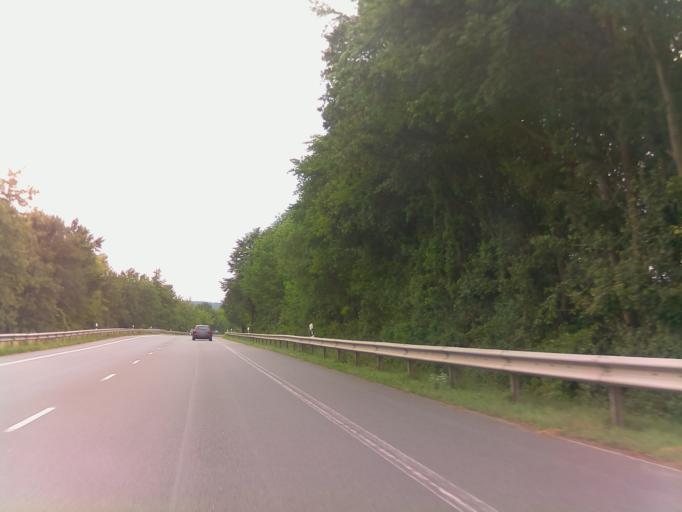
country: DE
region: North Rhine-Westphalia
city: Brakel
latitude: 51.7131
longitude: 9.1680
